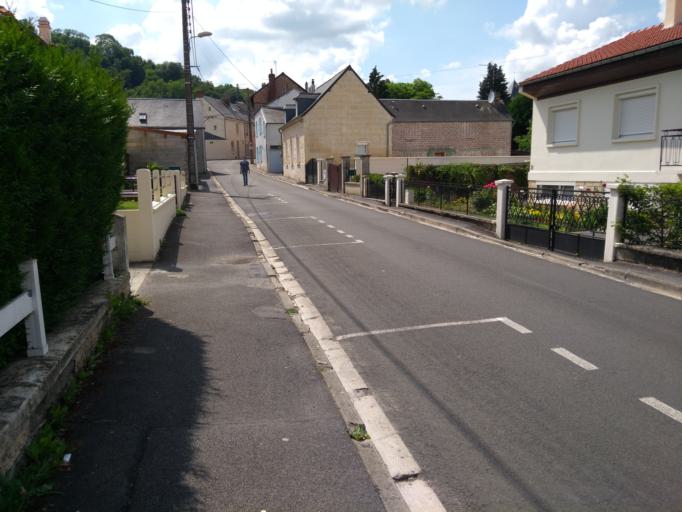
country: FR
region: Picardie
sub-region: Departement de l'Aisne
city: Laon
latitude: 49.5675
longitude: 3.6378
